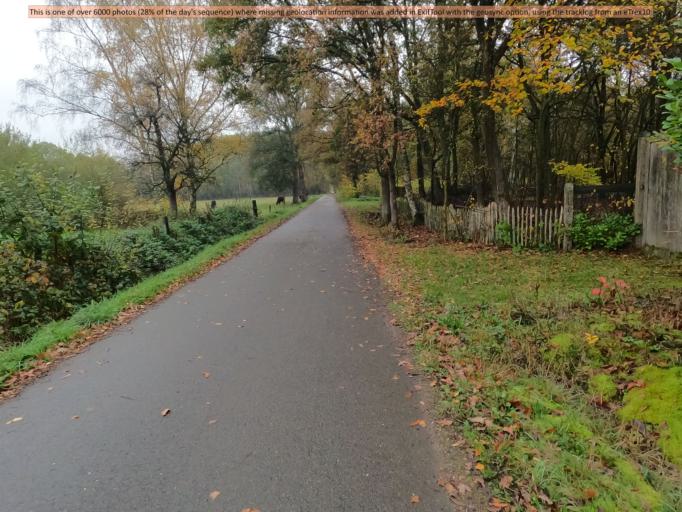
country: BE
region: Flanders
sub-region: Provincie Antwerpen
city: Lier
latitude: 51.1525
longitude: 4.6059
